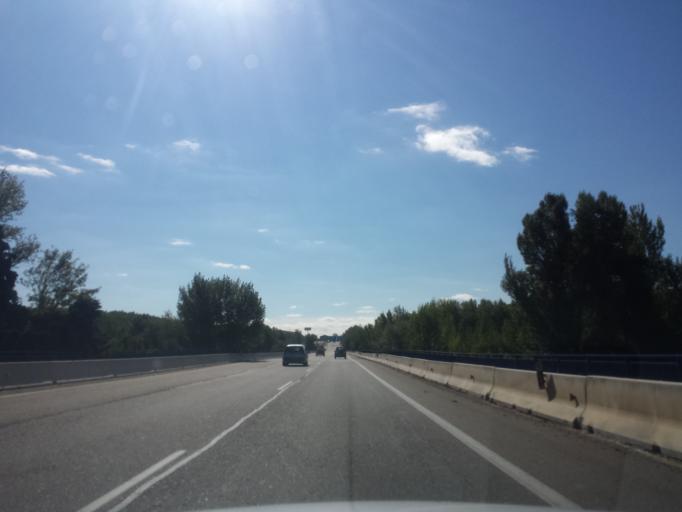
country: ES
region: Castille and Leon
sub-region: Provincia de Zamora
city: Castrogonzalo
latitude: 41.9844
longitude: -5.6272
